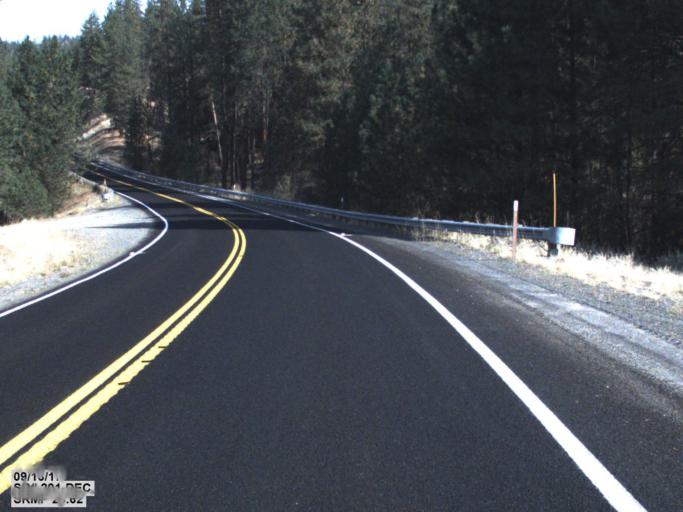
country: US
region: Washington
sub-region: Spokane County
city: Deer Park
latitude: 47.8703
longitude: -117.7063
